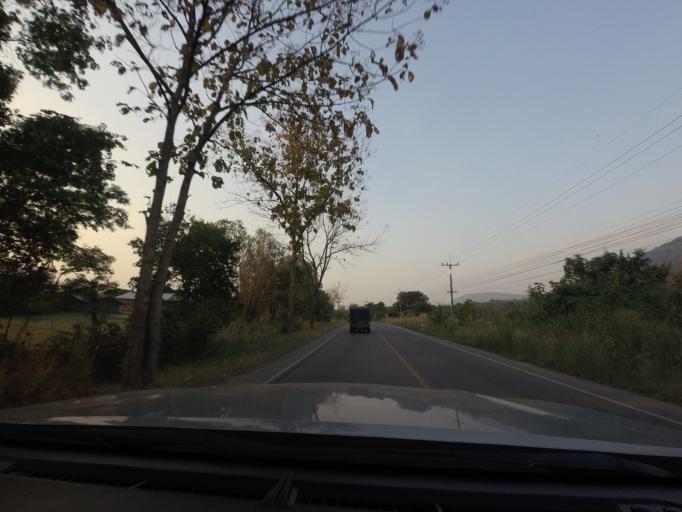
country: TH
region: Phitsanulok
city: Wang Thong
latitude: 16.7245
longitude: 100.4608
